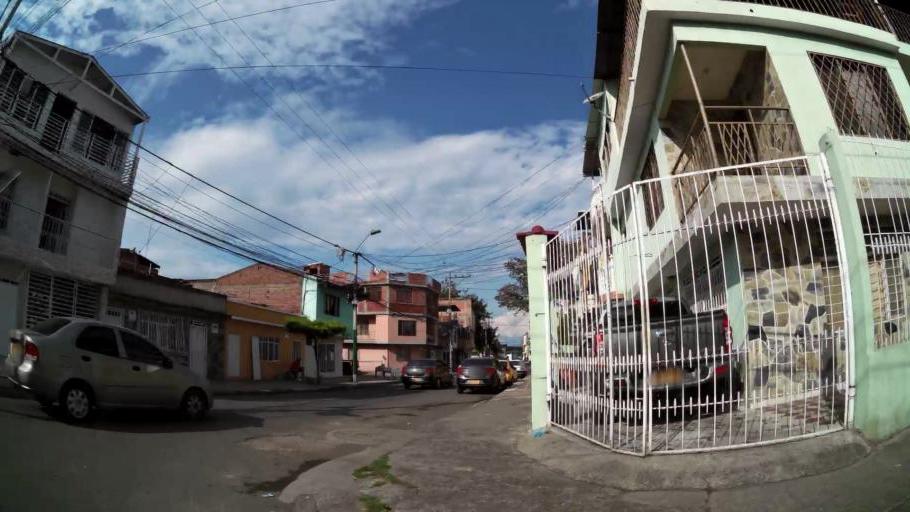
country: CO
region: Valle del Cauca
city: Cali
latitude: 3.4708
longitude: -76.5116
